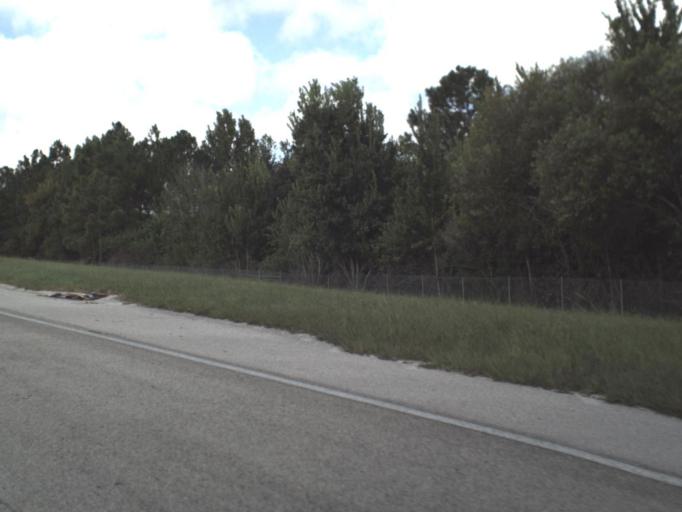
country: US
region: Florida
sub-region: Polk County
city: Gibsonia
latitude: 28.0997
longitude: -81.9501
